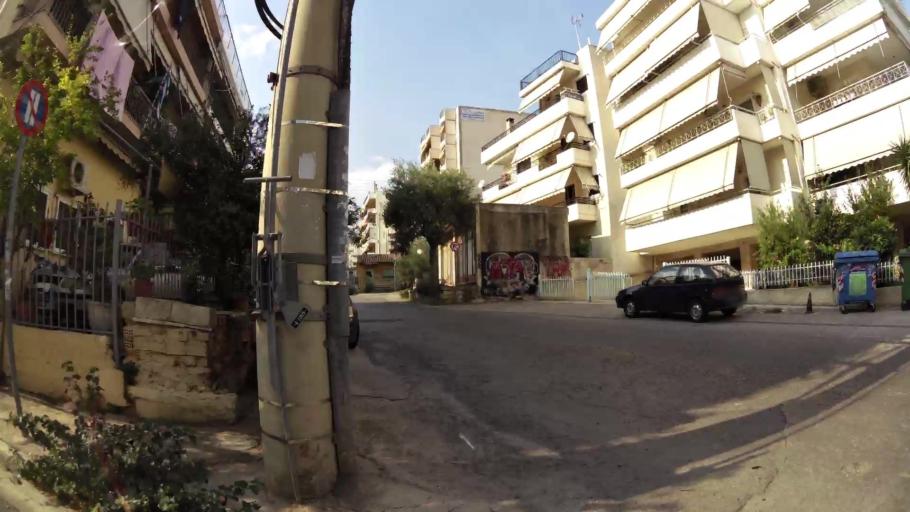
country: GR
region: Attica
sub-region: Nomarchia Athinas
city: Petroupolis
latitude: 38.0435
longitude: 23.6936
